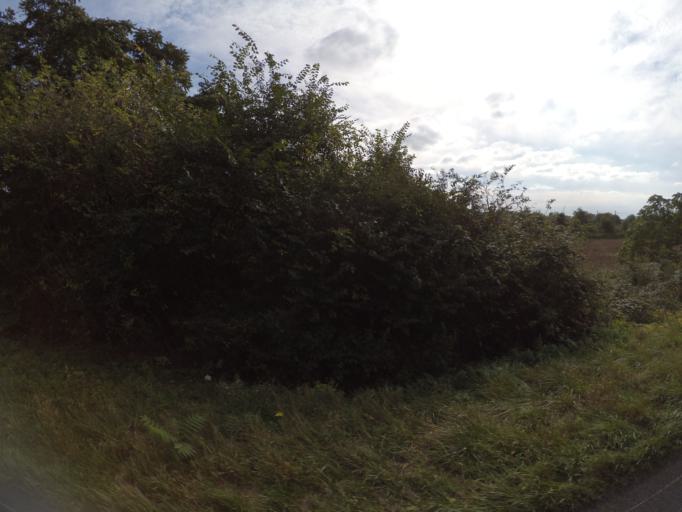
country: FR
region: Centre
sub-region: Departement d'Indre-et-Loire
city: Langeais
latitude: 47.3165
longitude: 0.3855
